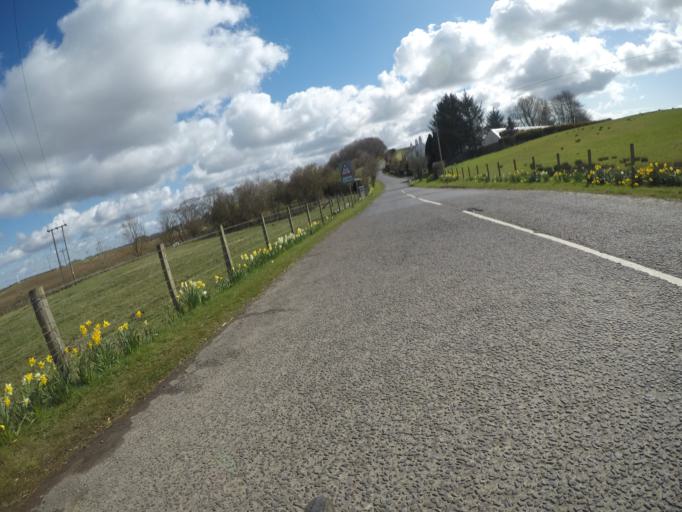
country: GB
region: Scotland
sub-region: East Ayrshire
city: Crosshouse
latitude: 55.5919
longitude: -4.5536
